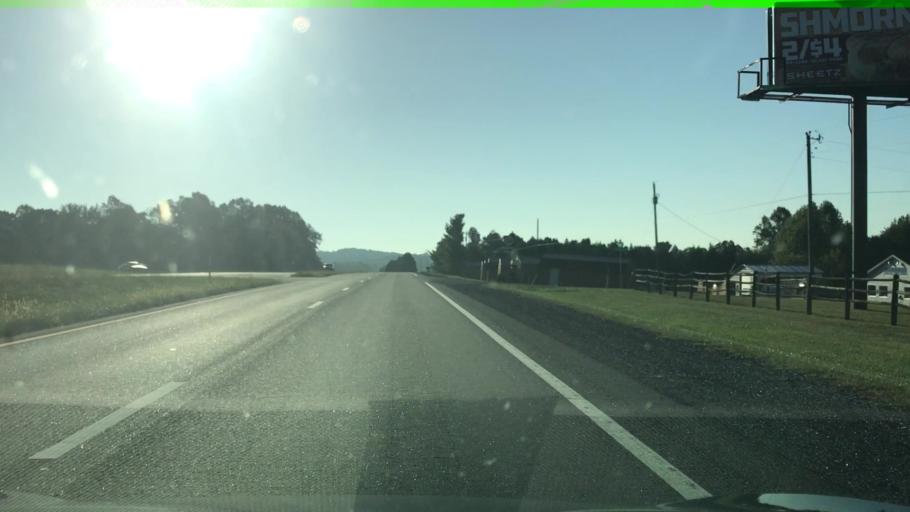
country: US
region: Virginia
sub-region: City of Bedford
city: Bedford
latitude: 37.3141
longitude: -79.4077
